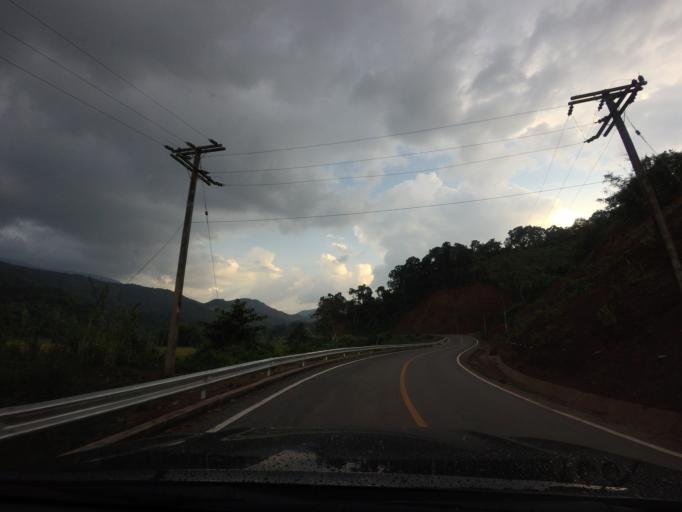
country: TH
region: Nan
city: Bo Kluea
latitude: 19.2237
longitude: 101.1825
